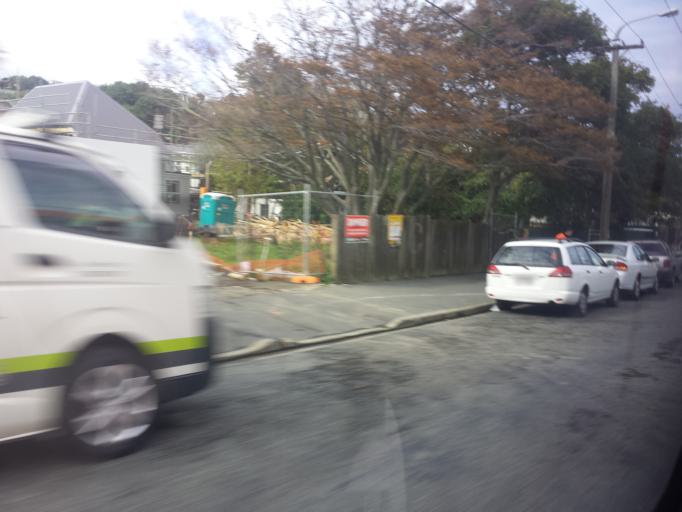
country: NZ
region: Wellington
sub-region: Wellington City
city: Wellington
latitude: -41.3066
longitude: 174.7932
